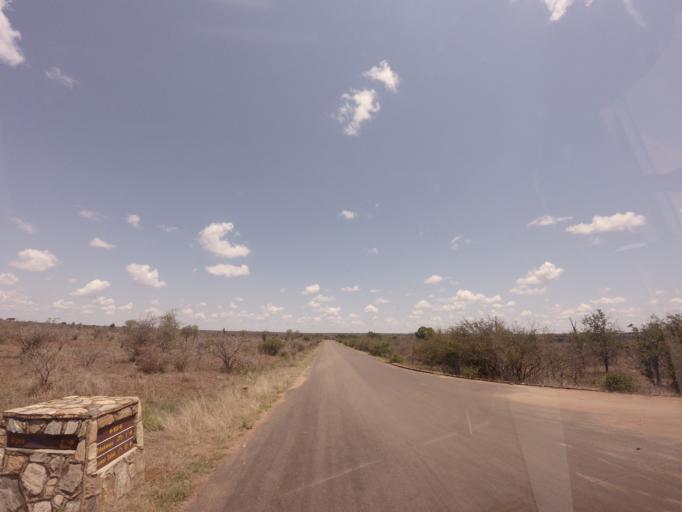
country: ZA
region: Mpumalanga
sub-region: Ehlanzeni District
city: Komatipoort
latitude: -24.8005
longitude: 31.8740
